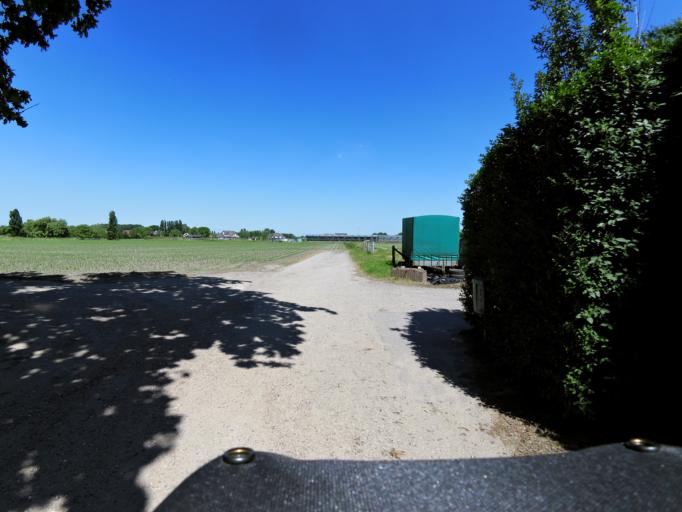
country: NL
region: South Holland
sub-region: Gemeente Hellevoetsluis
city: Nieuw-Helvoet
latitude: 51.8825
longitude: 4.0669
